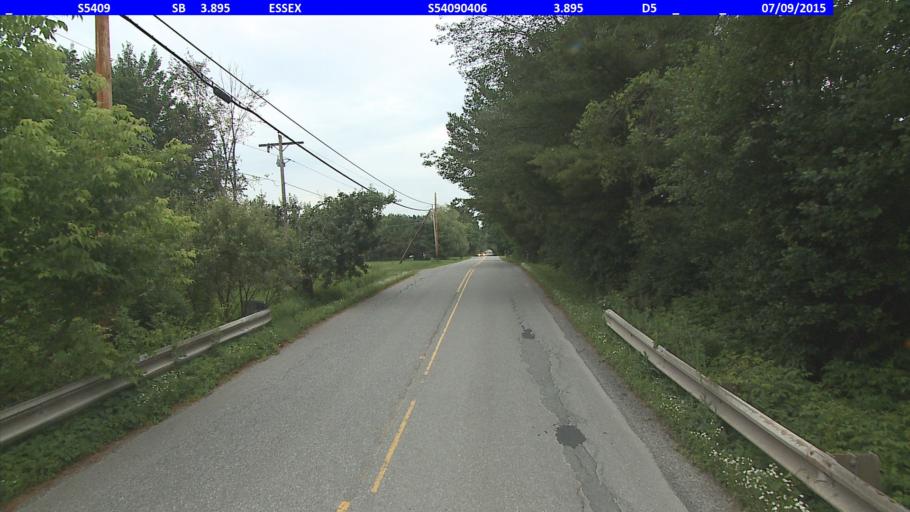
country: US
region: Vermont
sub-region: Chittenden County
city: Essex Junction
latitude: 44.5633
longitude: -73.0629
